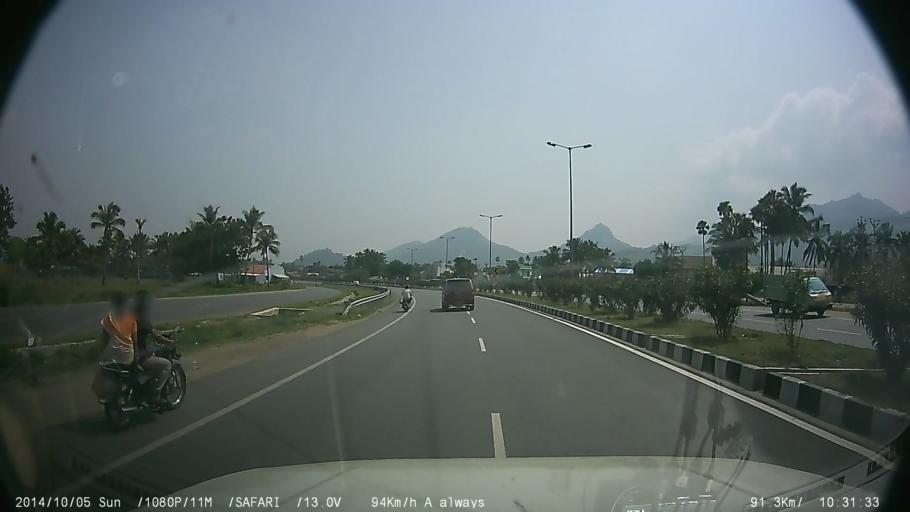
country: IN
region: Tamil Nadu
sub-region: Salem
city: Salem
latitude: 11.6281
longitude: 78.1643
